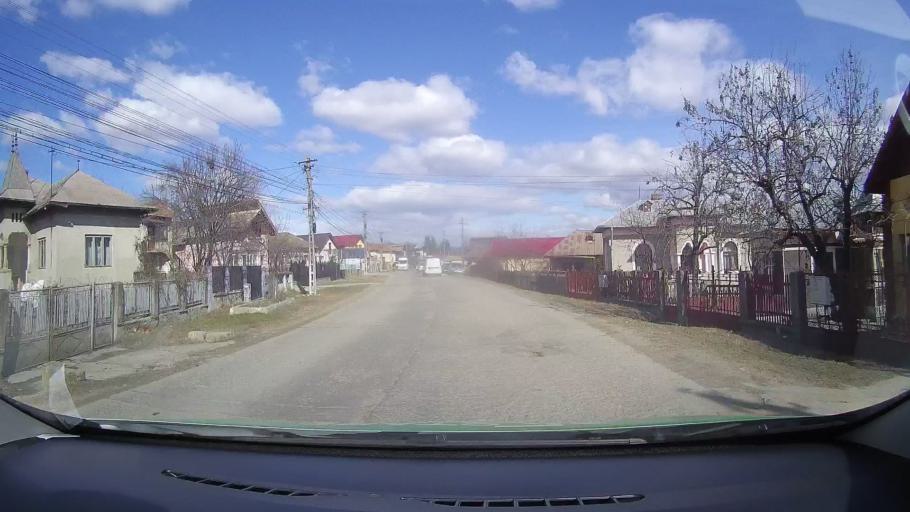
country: RO
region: Dambovita
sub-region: Comuna Branesti
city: Branesti
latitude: 45.0289
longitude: 25.4098
